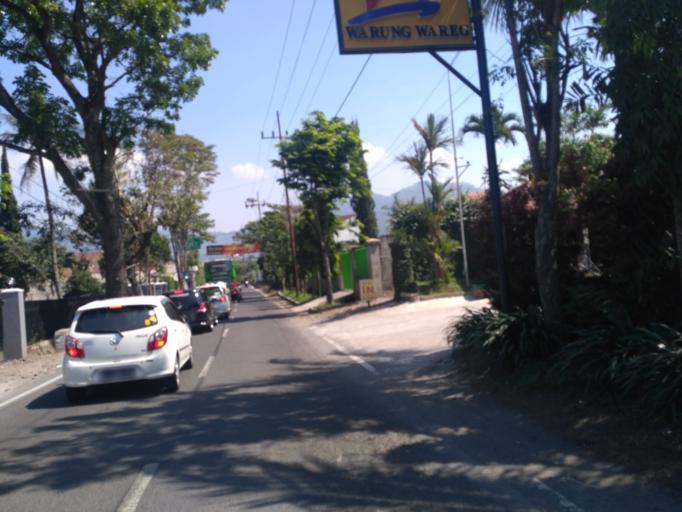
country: ID
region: East Java
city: Batu
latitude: -7.8631
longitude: 112.5289
